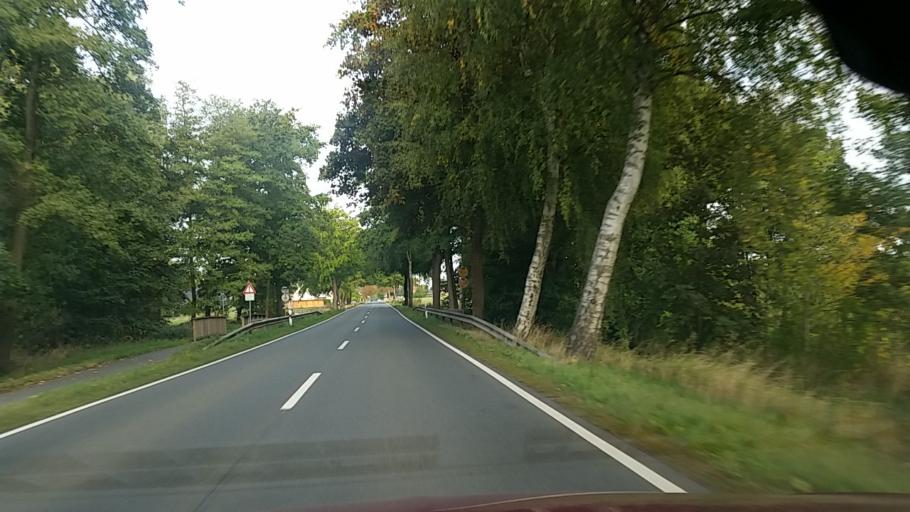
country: DE
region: Lower Saxony
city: Ahnsbeck
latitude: 52.6031
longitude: 10.2986
